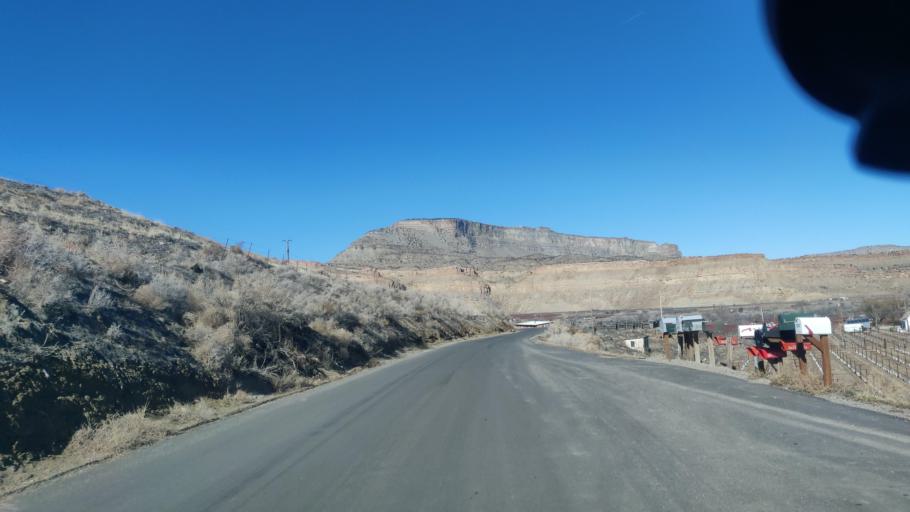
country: US
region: Colorado
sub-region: Mesa County
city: Palisade
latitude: 39.0998
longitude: -108.3305
